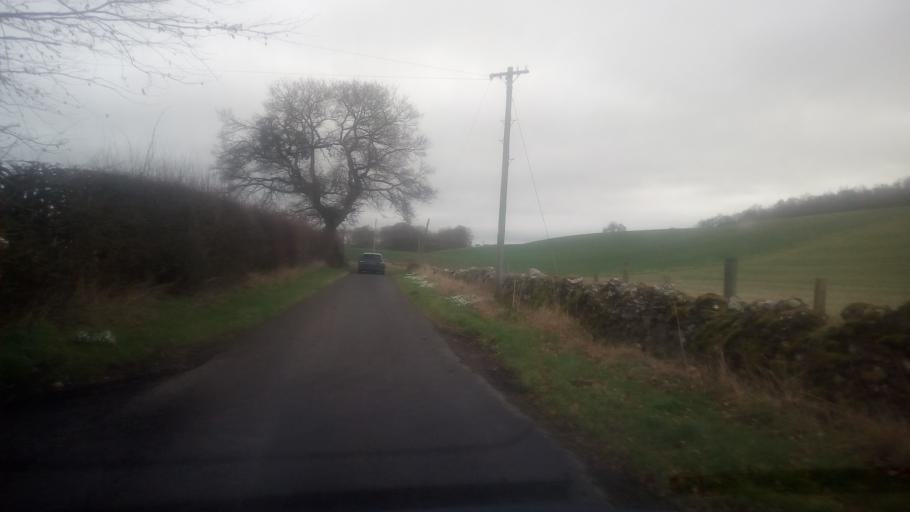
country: GB
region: Scotland
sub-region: The Scottish Borders
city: Jedburgh
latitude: 55.5030
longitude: -2.5372
